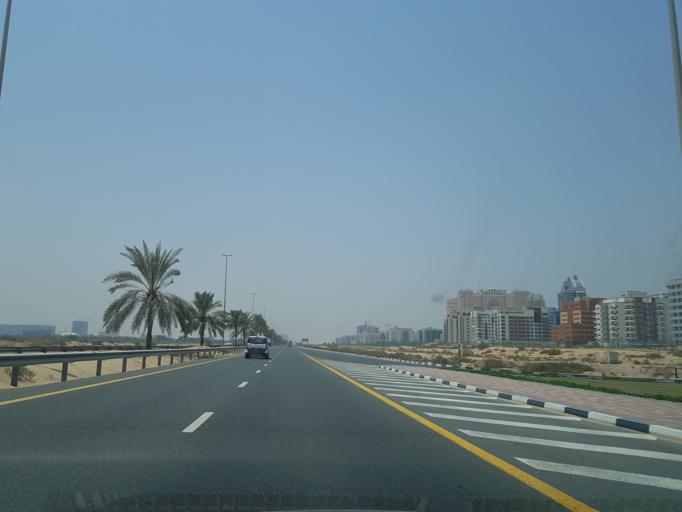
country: AE
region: Ash Shariqah
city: Sharjah
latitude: 25.1198
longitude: 55.4006
